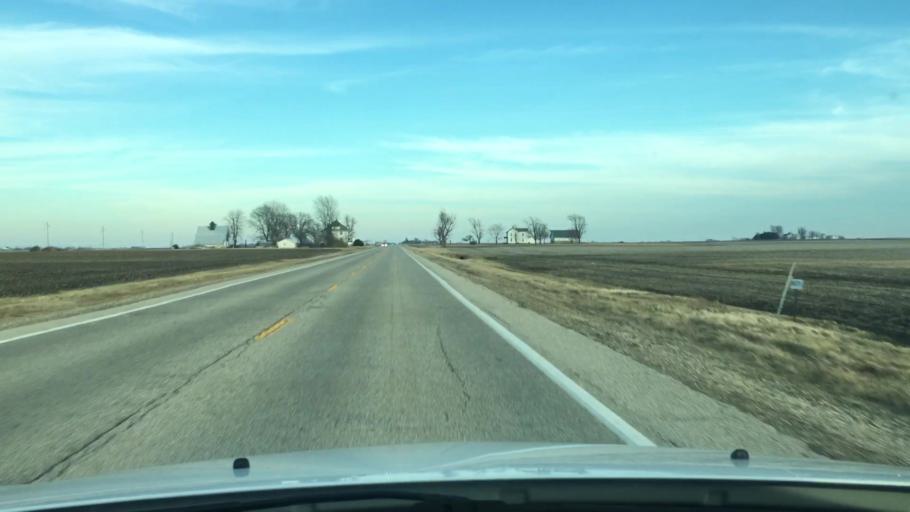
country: US
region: Illinois
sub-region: Woodford County
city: El Paso
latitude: 40.7385
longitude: -88.9548
